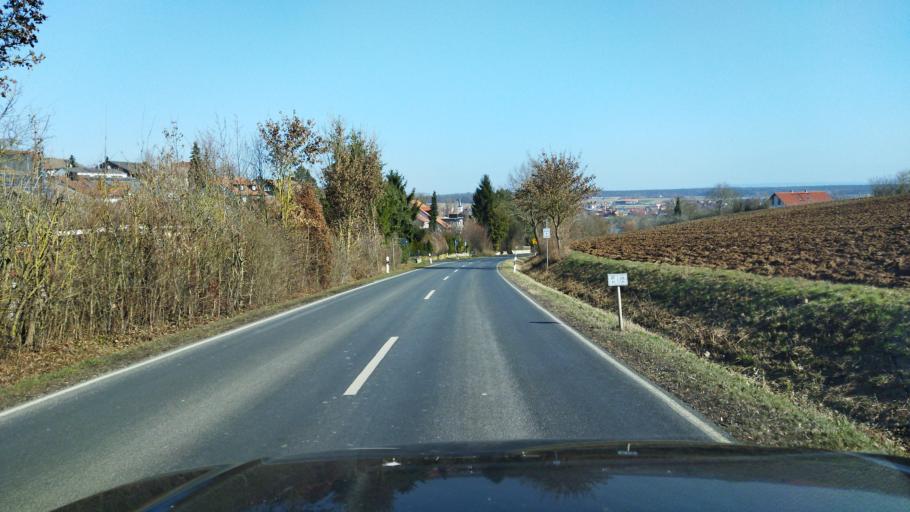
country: DE
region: Bavaria
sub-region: Regierungsbezirk Unterfranken
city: Buchbrunn
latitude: 49.7650
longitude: 10.1468
